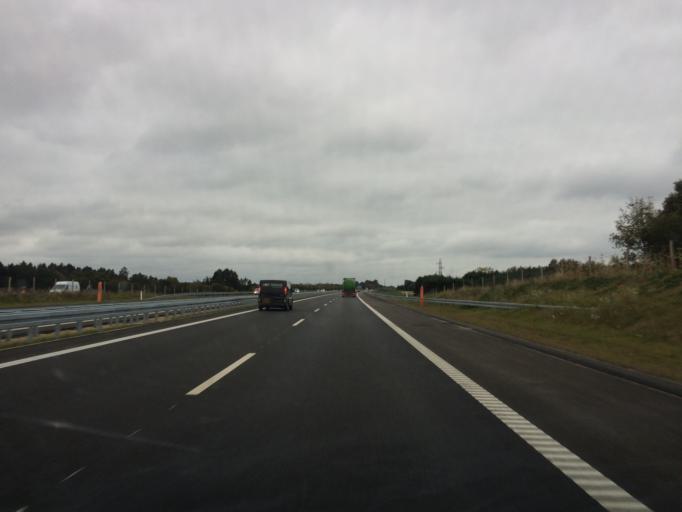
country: DK
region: Central Jutland
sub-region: Silkeborg Kommune
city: Silkeborg
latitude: 56.1665
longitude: 9.4706
